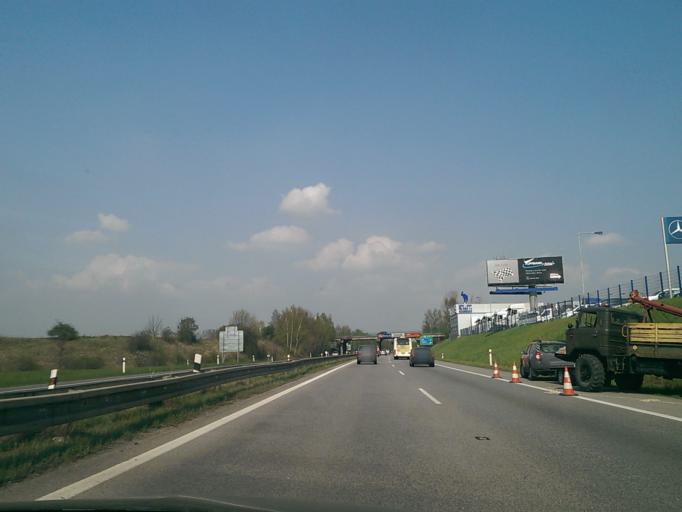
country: CZ
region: Central Bohemia
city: Brandys nad Labem-Stara Boleslav
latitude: 50.1678
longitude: 14.6718
